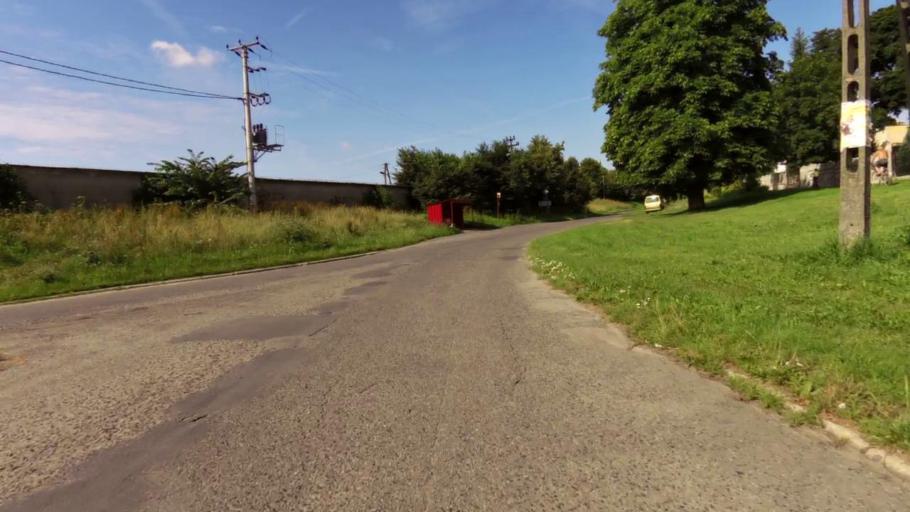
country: PL
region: West Pomeranian Voivodeship
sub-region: Powiat stargardzki
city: Marianowo
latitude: 53.3400
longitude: 15.1911
